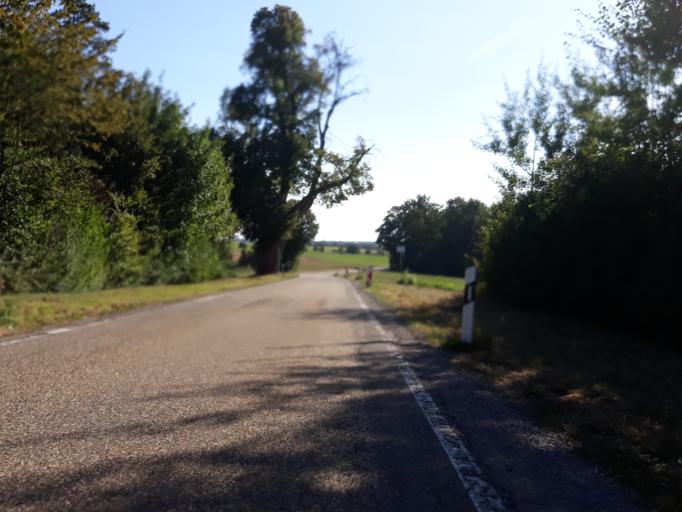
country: DE
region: Baden-Wuerttemberg
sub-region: Regierungsbezirk Stuttgart
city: Deckenpfronn
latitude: 48.6649
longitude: 8.8409
